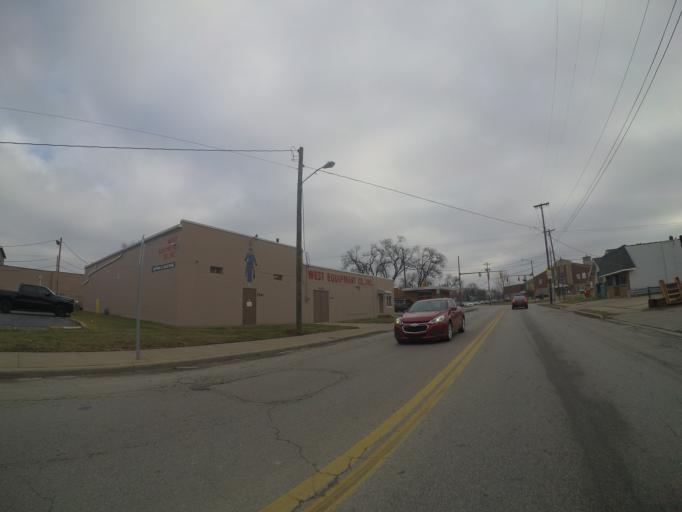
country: US
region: Ohio
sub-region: Lucas County
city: Oregon
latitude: 41.6226
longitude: -83.5153
